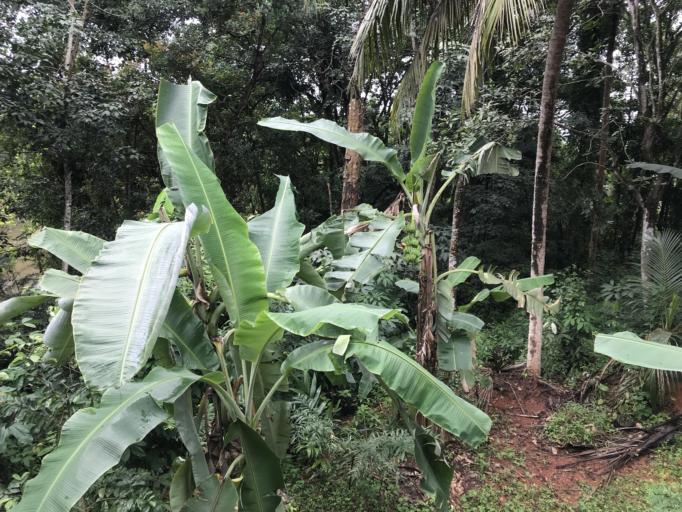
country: LK
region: Western
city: Gampaha
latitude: 7.1011
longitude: 79.9772
